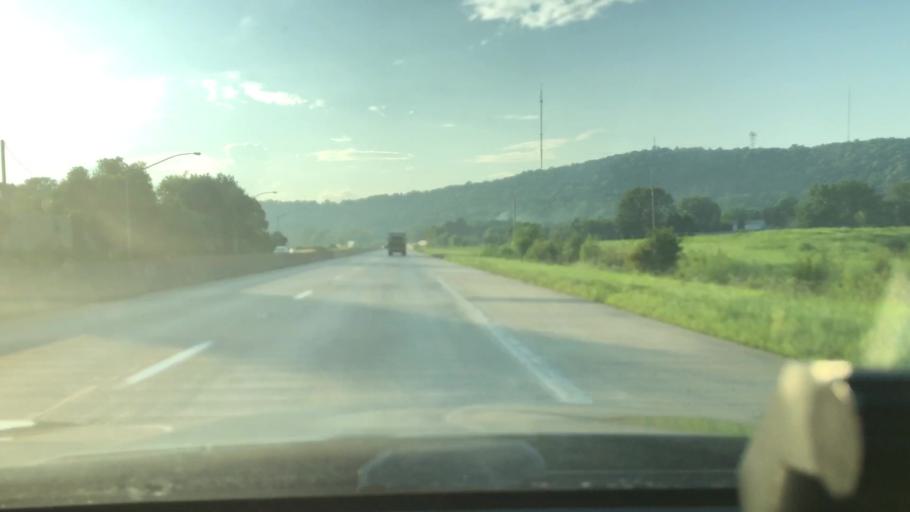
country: US
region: Pennsylvania
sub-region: Lehigh County
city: Coopersburg
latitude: 40.5522
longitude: -75.4288
